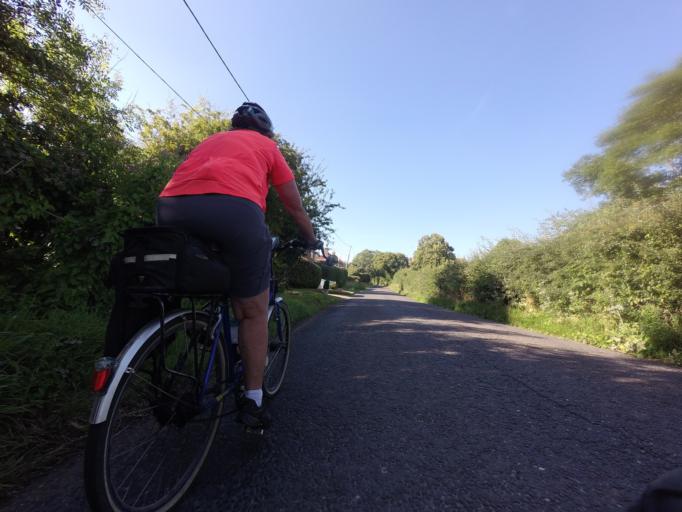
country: GB
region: England
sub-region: Kent
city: Tenterden
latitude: 51.0385
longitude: 0.6991
